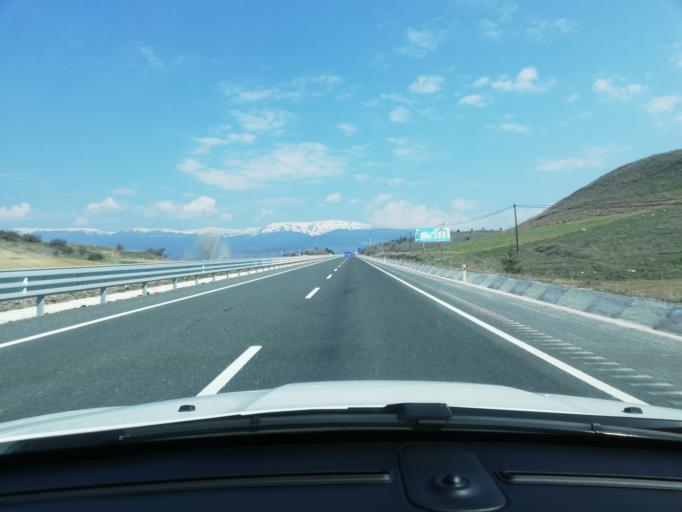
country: TR
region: Cankiri
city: Ilgaz
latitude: 40.9127
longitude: 33.6492
